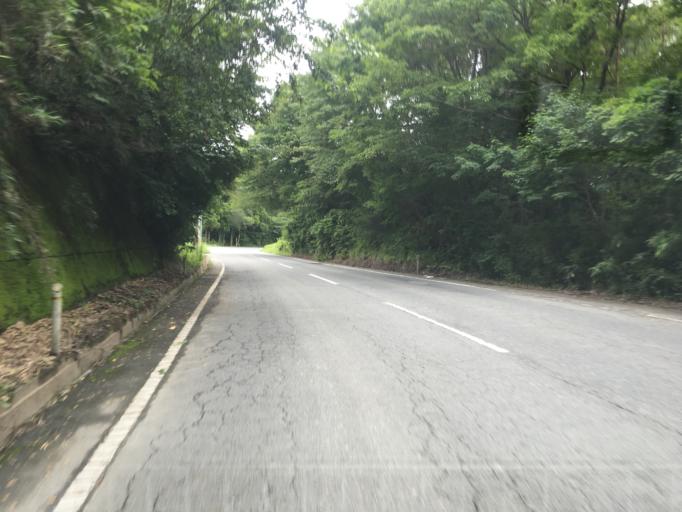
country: JP
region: Miyagi
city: Marumori
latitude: 37.7428
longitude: 140.9317
